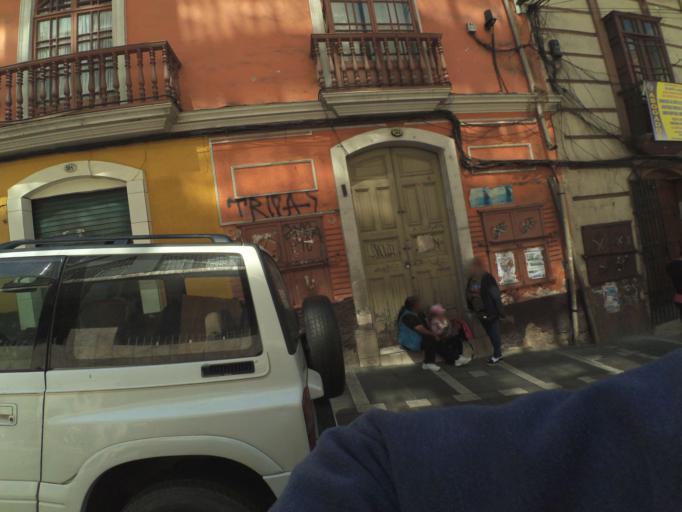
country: BO
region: La Paz
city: La Paz
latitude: -16.4950
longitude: -68.1346
